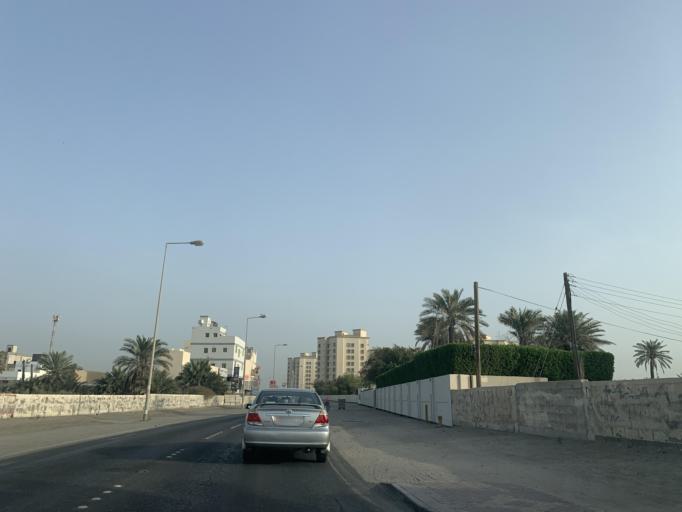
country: BH
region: Northern
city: Madinat `Isa
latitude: 26.1816
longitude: 50.5600
